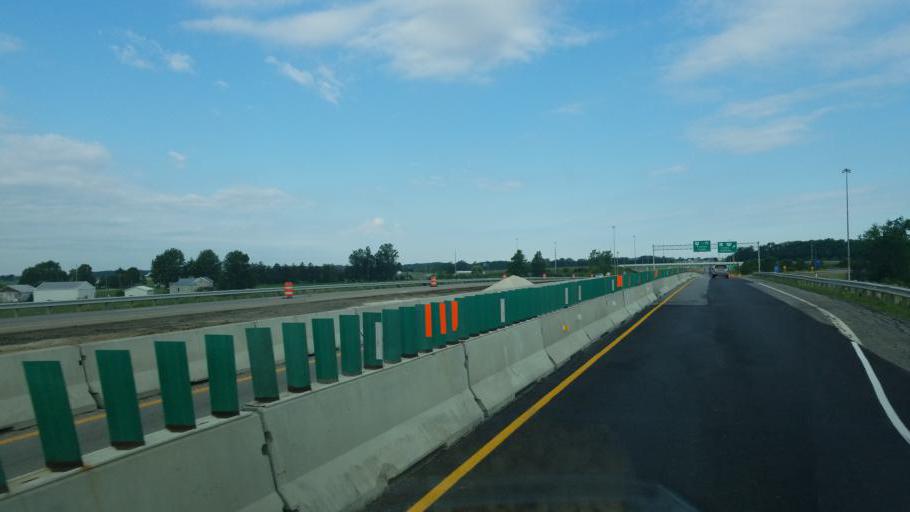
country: US
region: Ohio
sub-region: Wyandot County
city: Carey
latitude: 40.9386
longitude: -83.3950
